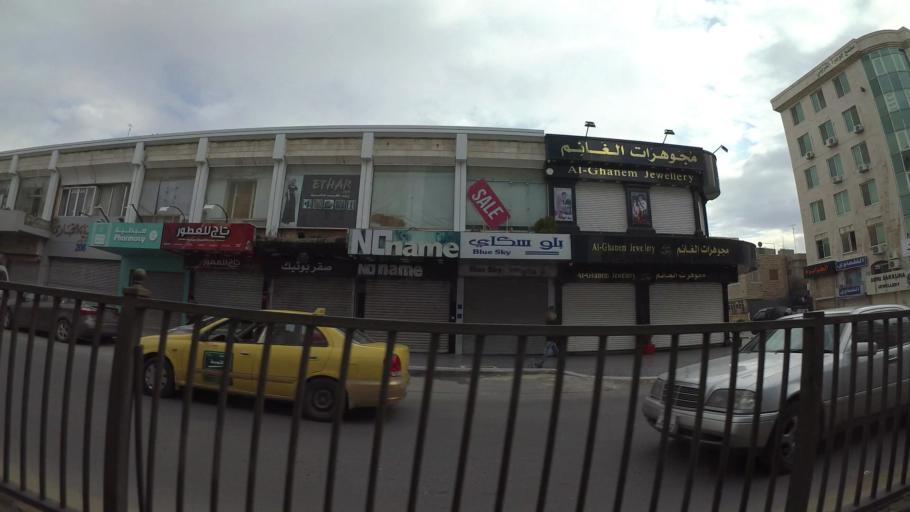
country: JO
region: Amman
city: Amman
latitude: 31.9686
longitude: 35.9162
